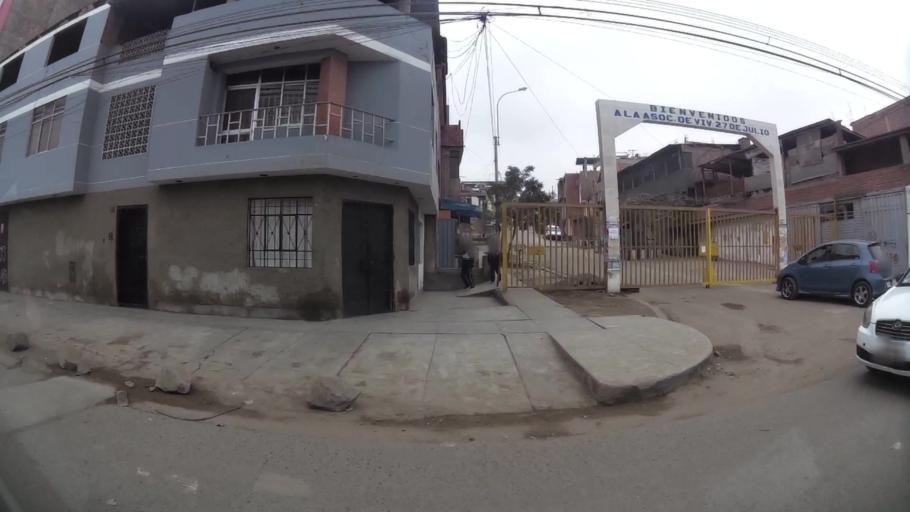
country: PE
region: Lima
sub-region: Lima
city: Surco
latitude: -12.1719
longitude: -76.9620
